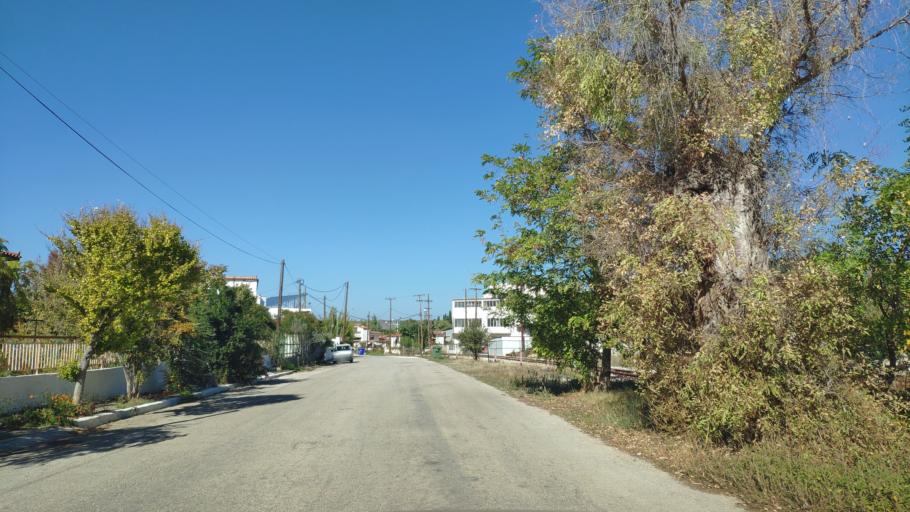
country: GR
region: Peloponnese
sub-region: Nomos Korinthias
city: Khiliomodhi
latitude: 37.8068
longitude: 22.8677
